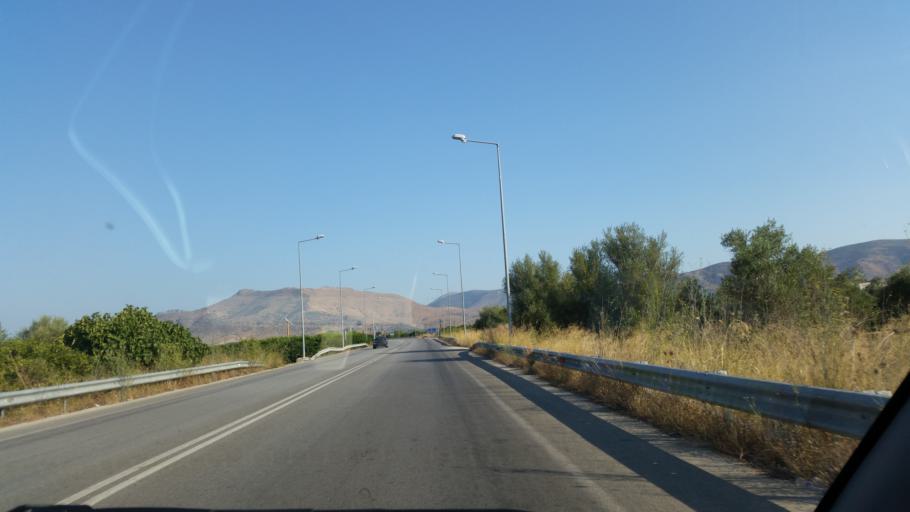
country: GR
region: Peloponnese
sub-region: Nomos Argolidos
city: Ayia Trias
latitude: 37.6367
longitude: 22.8169
